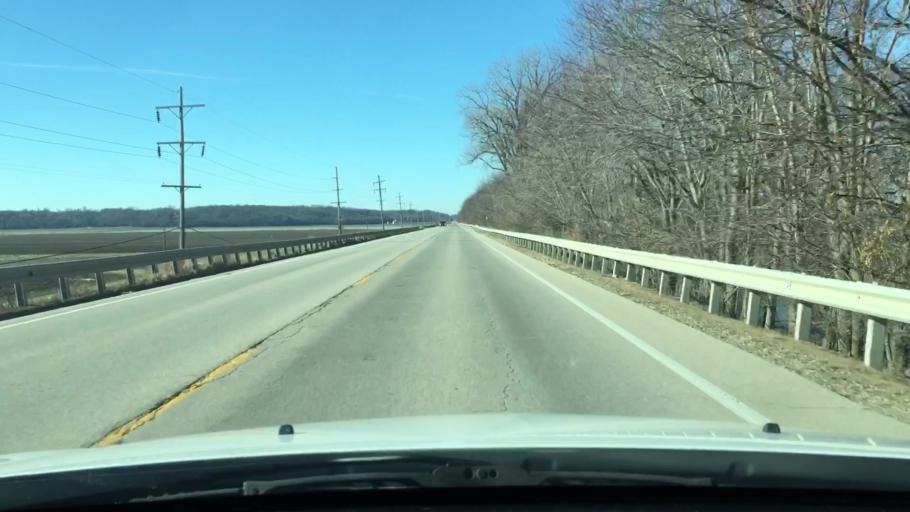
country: US
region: Illinois
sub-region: Mason County
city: Havana
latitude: 40.2996
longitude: -90.1033
